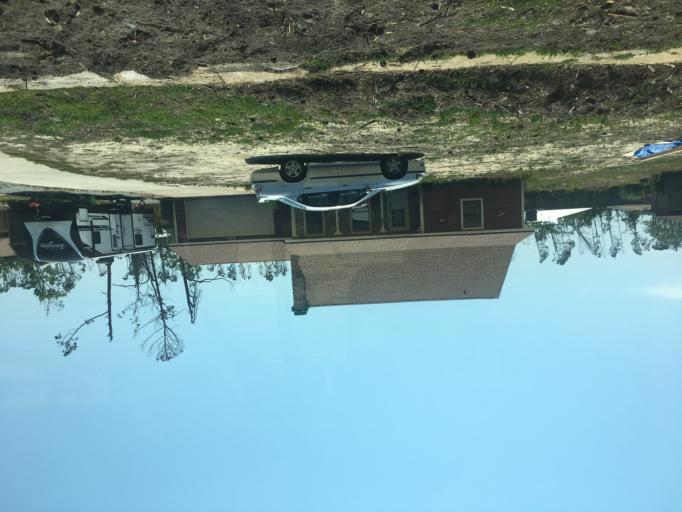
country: US
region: Florida
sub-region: Bay County
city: Lynn Haven
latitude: 30.2209
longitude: -85.6557
